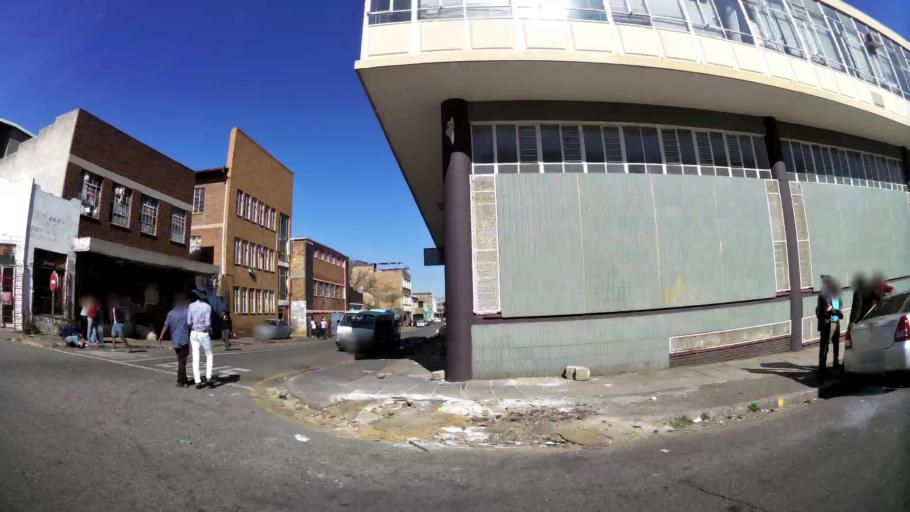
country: ZA
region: Gauteng
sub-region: City of Johannesburg Metropolitan Municipality
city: Johannesburg
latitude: -26.2061
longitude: 28.0619
